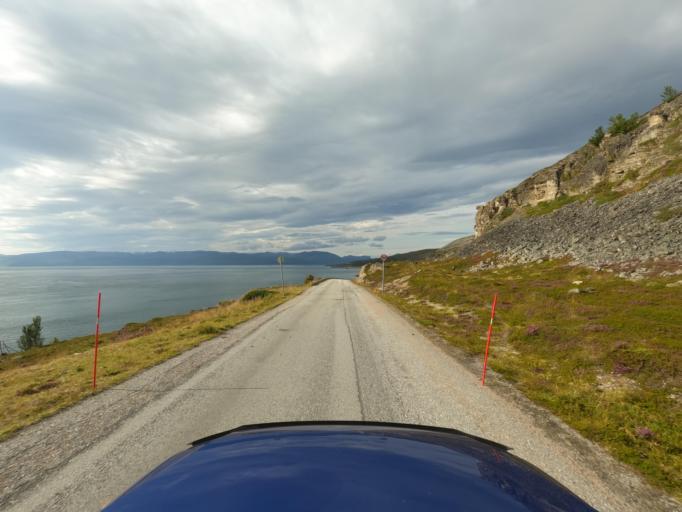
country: NO
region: Finnmark Fylke
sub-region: Kvalsund
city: Kvalsund
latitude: 70.5068
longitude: 23.8890
